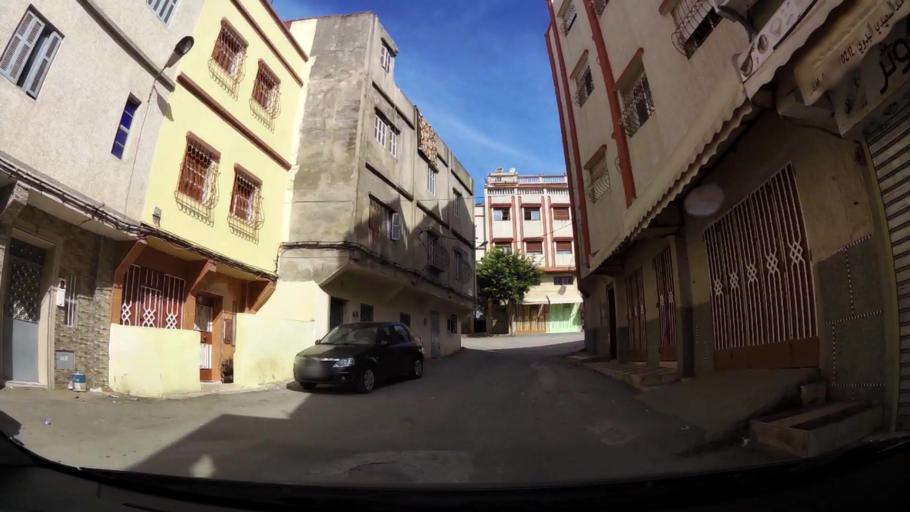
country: MA
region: Tanger-Tetouan
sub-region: Tanger-Assilah
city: Tangier
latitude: 35.7696
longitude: -5.7692
